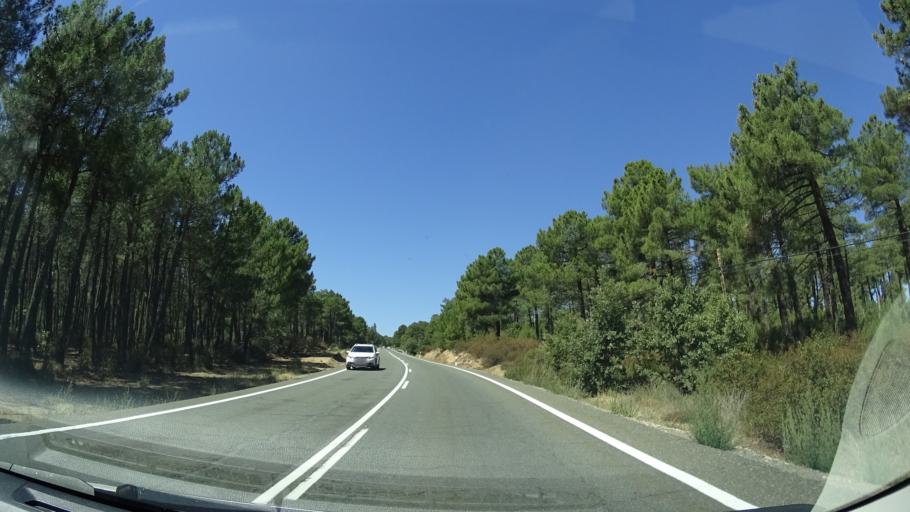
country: ES
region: Castille and Leon
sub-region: Provincia de Avila
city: Las Navas del Marques
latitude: 40.5926
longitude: -4.3698
